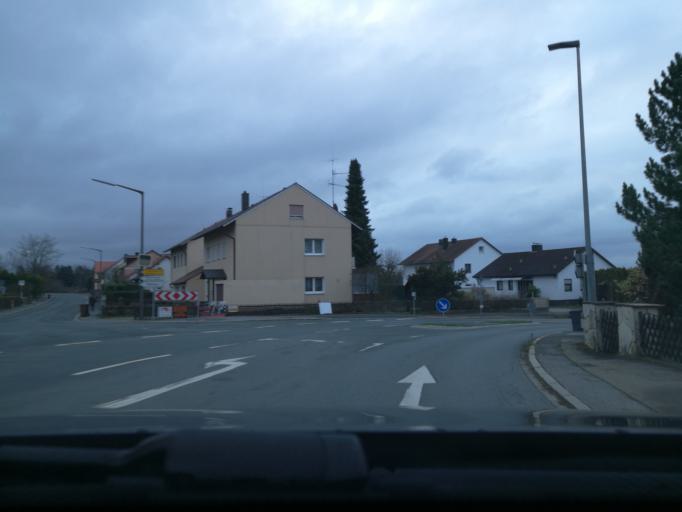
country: DE
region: Bavaria
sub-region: Regierungsbezirk Mittelfranken
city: Kalchreuth
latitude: 49.5573
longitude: 11.1391
